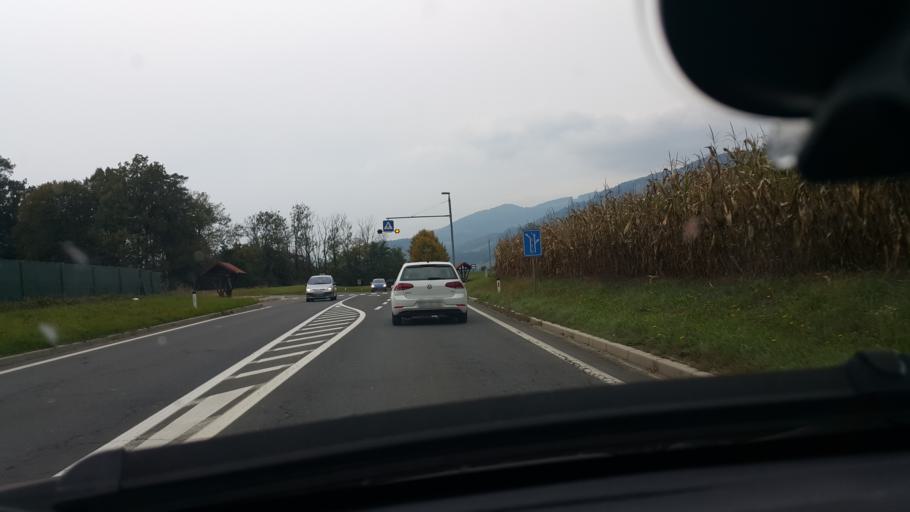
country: SI
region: Radlje ob Dravi
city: Radlje ob Dravi
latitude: 46.6142
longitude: 15.2025
